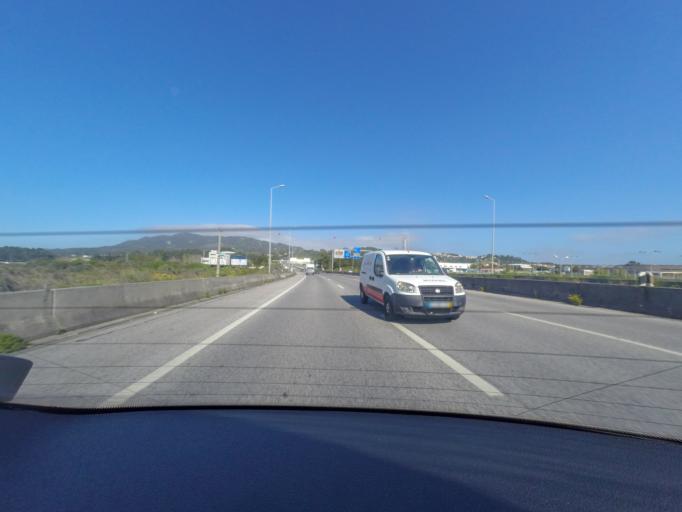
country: PT
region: Lisbon
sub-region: Sintra
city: Sintra
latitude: 38.7809
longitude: -9.3568
